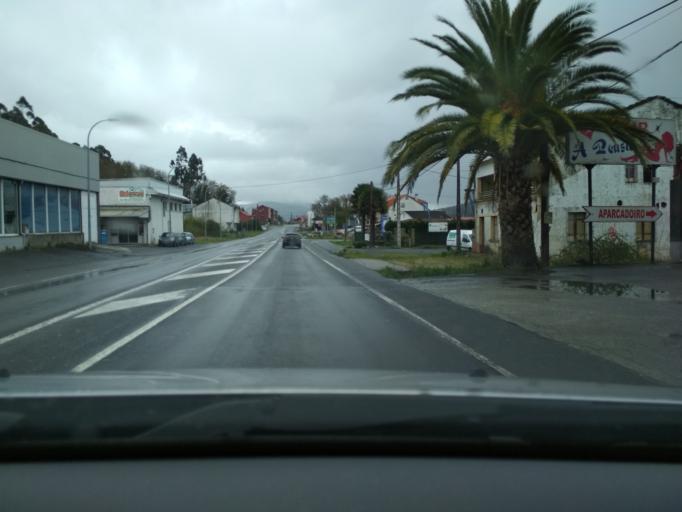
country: ES
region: Galicia
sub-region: Provincia da Coruna
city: Padron
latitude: 42.7551
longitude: -8.6522
